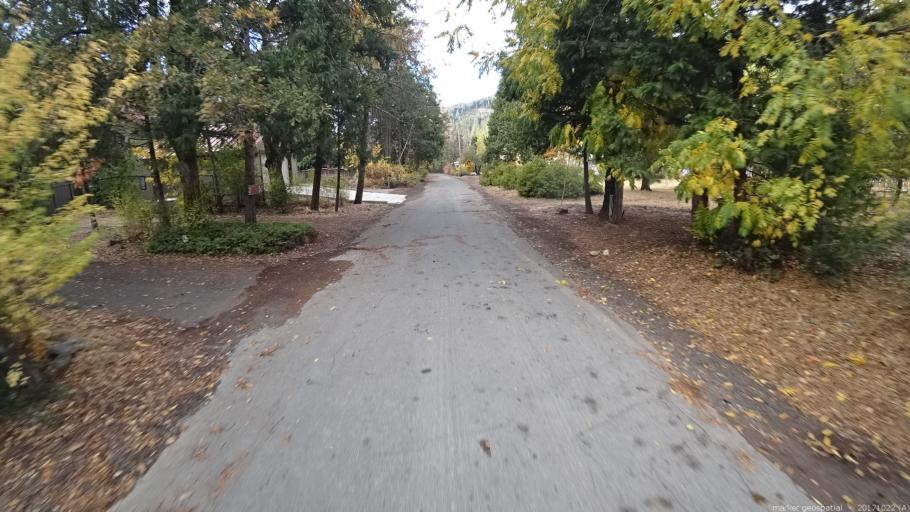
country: US
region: California
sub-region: Siskiyou County
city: Dunsmuir
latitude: 41.1406
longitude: -122.3153
